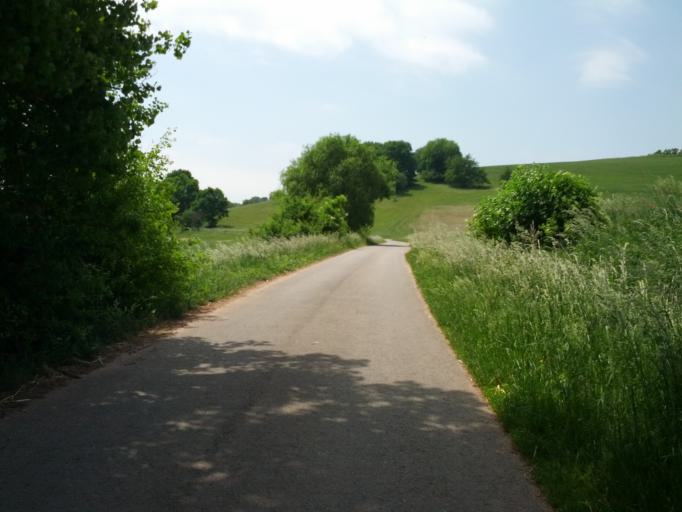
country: DE
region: Thuringia
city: Urnshausen
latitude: 50.7283
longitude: 10.1662
